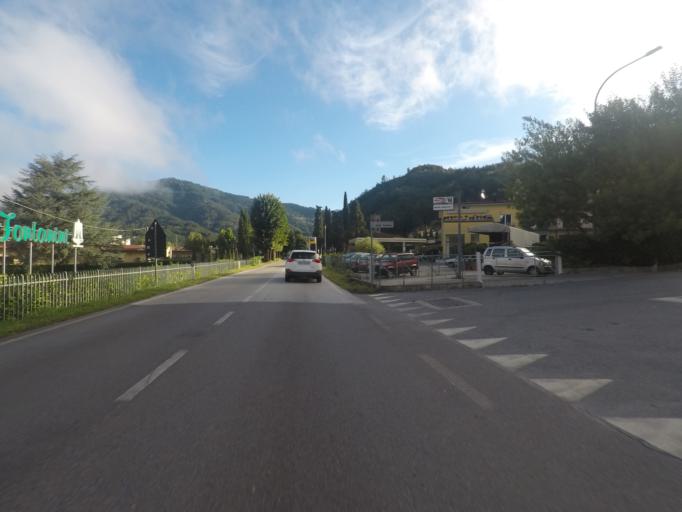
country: IT
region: Tuscany
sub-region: Provincia di Lucca
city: Bagni di Lucca
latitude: 43.9978
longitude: 10.5574
